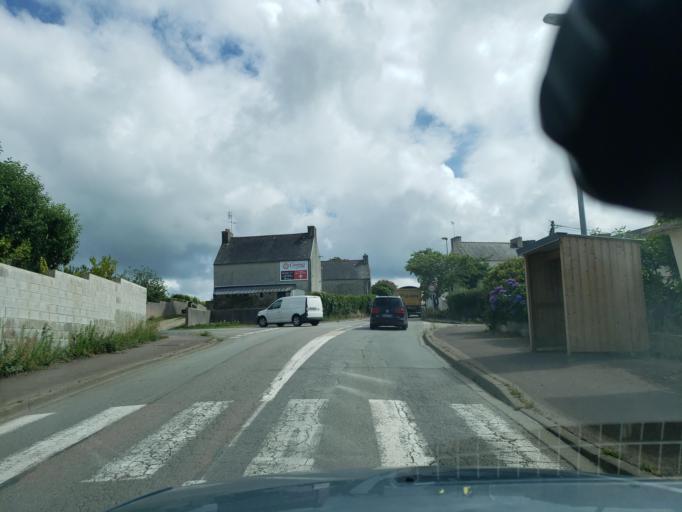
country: FR
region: Brittany
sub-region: Departement du Finistere
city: Ploneour-Lanvern
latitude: 47.9084
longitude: -4.2805
